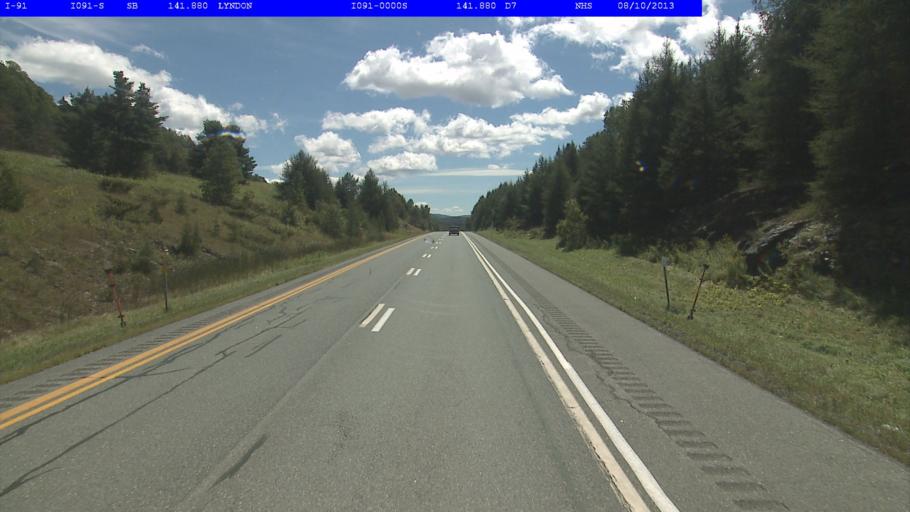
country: US
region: Vermont
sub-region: Caledonia County
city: Lyndonville
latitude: 44.5760
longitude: -72.0477
